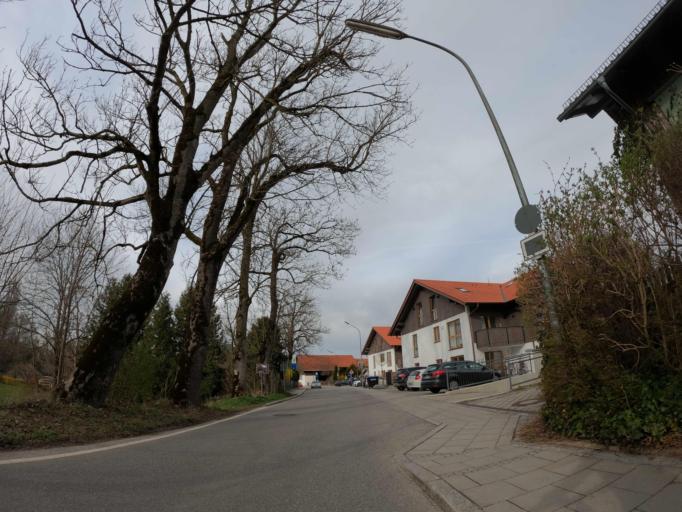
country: DE
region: Bavaria
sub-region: Upper Bavaria
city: Taufkirchen
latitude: 48.0405
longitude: 11.6212
